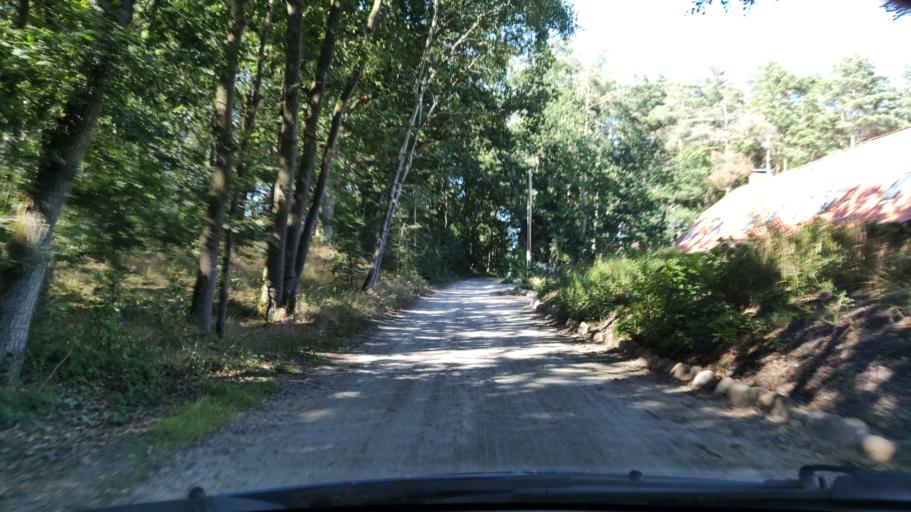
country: DE
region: Lower Saxony
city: Thomasburg
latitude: 53.1821
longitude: 10.6731
